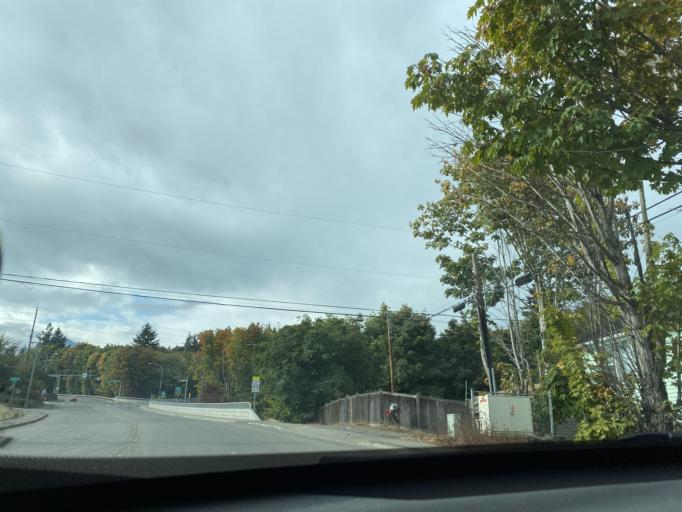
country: US
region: Washington
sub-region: Clallam County
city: Port Angeles
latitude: 48.1059
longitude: -123.4255
